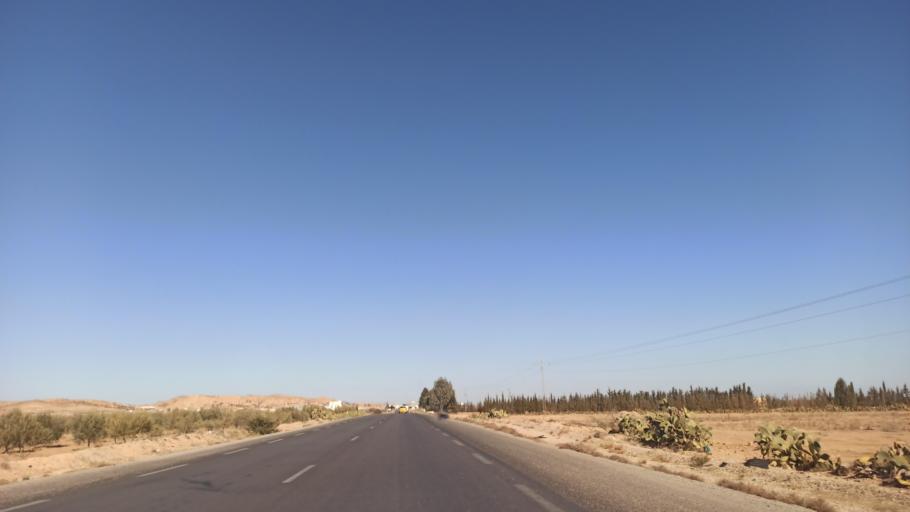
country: TN
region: Sidi Bu Zayd
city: Bi'r al Hufayy
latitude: 34.9059
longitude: 9.1784
